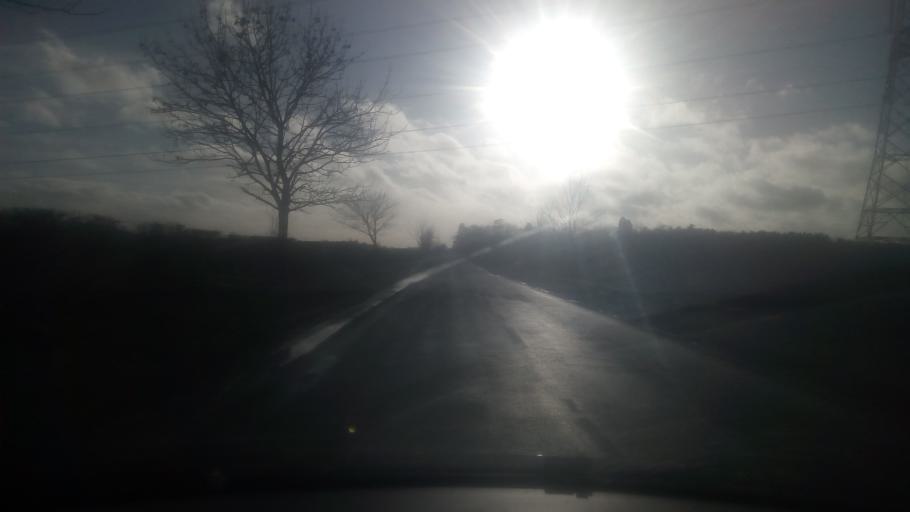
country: GB
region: Scotland
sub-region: The Scottish Borders
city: Coldstream
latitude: 55.6982
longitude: -2.3169
